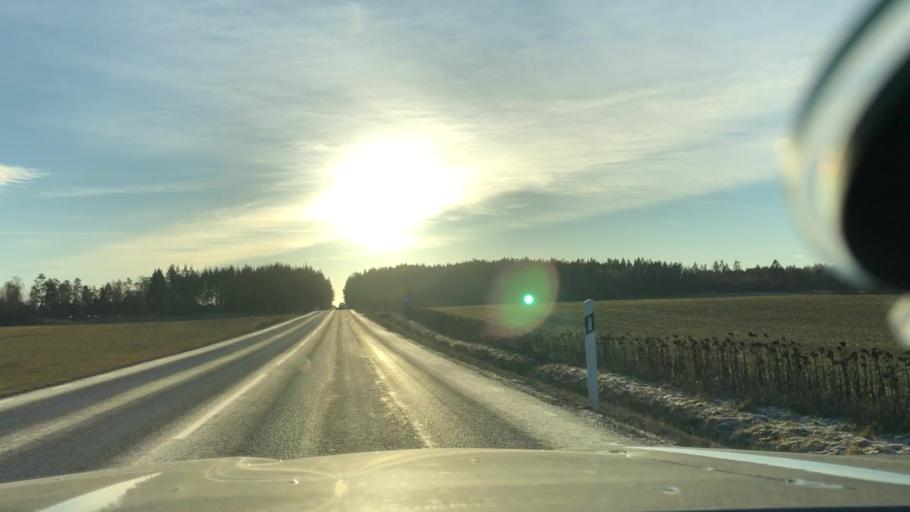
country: SE
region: Stockholm
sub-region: Sodertalje Kommun
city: Pershagen
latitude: 59.0481
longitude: 17.6069
